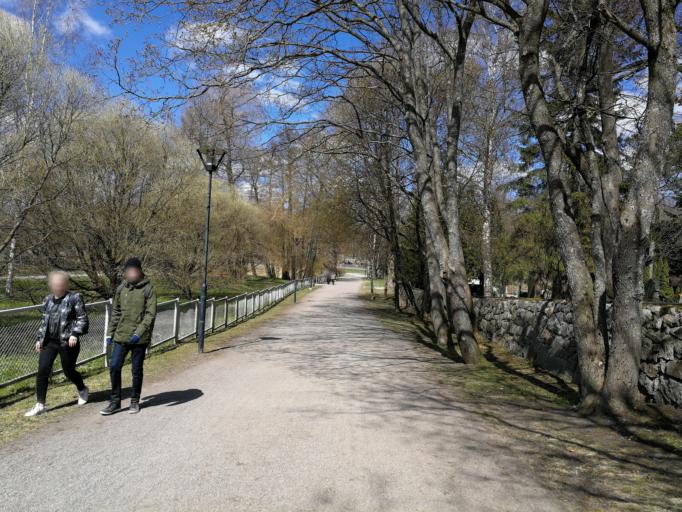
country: FI
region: Uusimaa
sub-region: Helsinki
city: Helsinki
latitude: 60.1680
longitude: 24.9164
